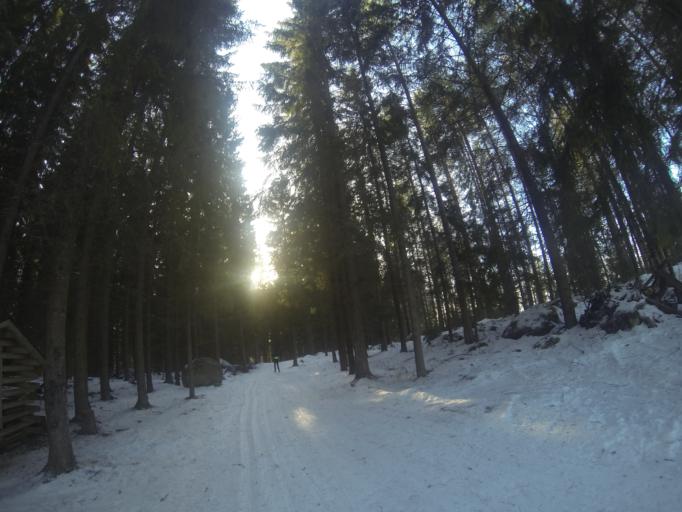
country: FI
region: Southern Savonia
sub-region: Savonlinna
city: Savonlinna
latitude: 61.9056
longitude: 28.9137
